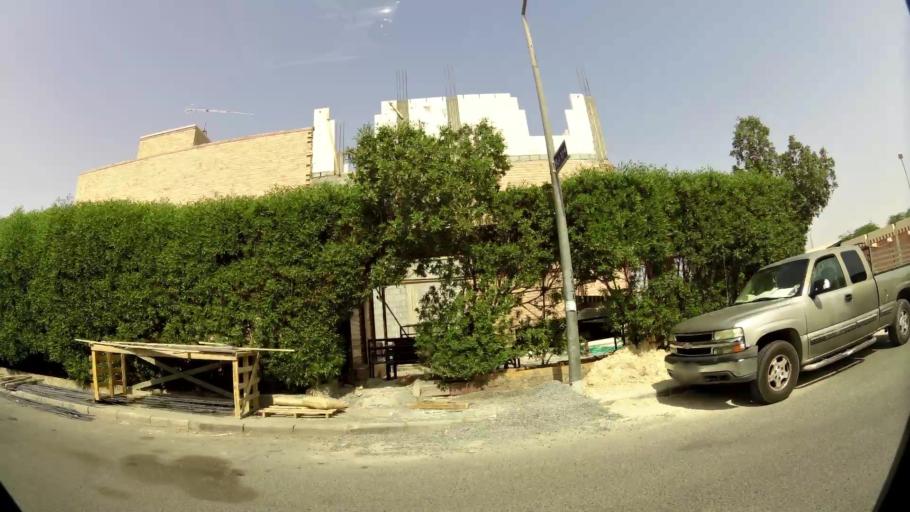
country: KW
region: Muhafazat al Jahra'
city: Al Jahra'
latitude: 29.3333
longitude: 47.6594
